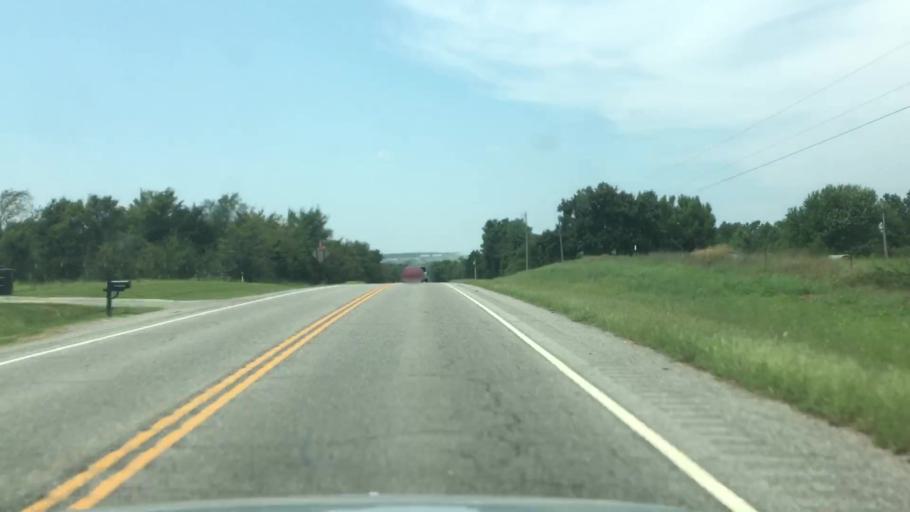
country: US
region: Oklahoma
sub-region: Muskogee County
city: Fort Gibson
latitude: 35.9369
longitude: -95.1936
